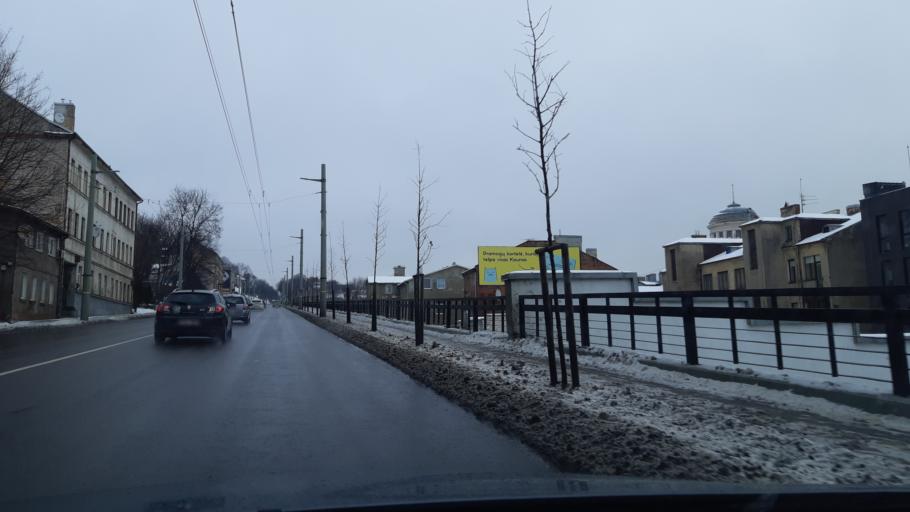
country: LT
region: Kauno apskritis
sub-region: Kaunas
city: Kaunas
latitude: 54.8990
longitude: 23.9032
